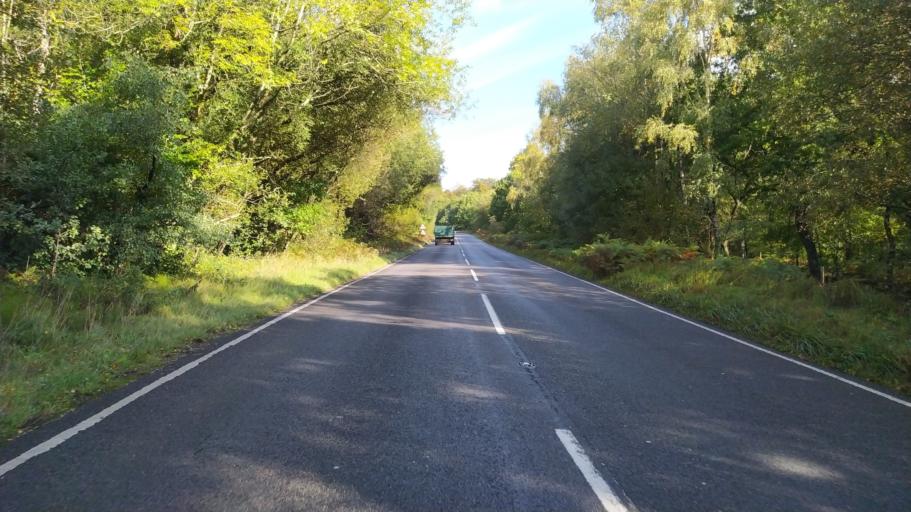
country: GB
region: England
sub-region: Hampshire
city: Cadnam
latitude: 50.9006
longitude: -1.5796
